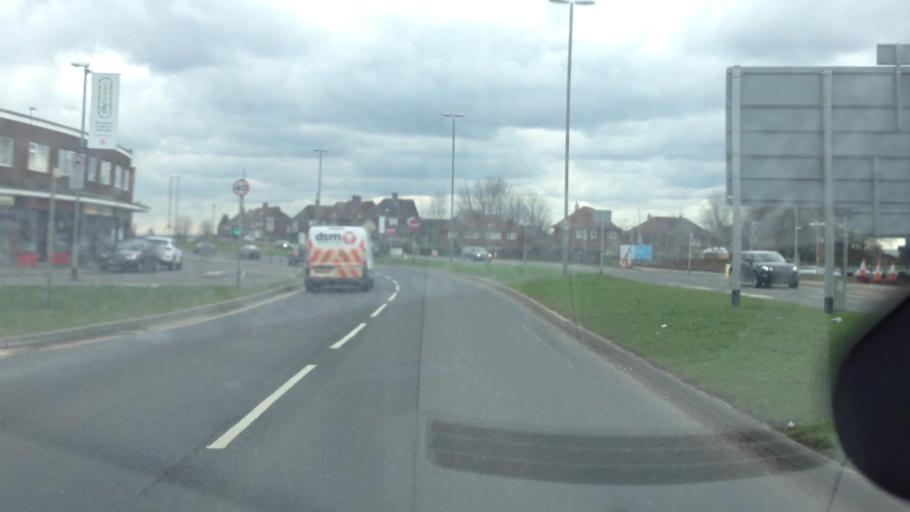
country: GB
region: England
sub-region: City and Borough of Leeds
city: Scholes
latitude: 53.8146
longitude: -1.4545
